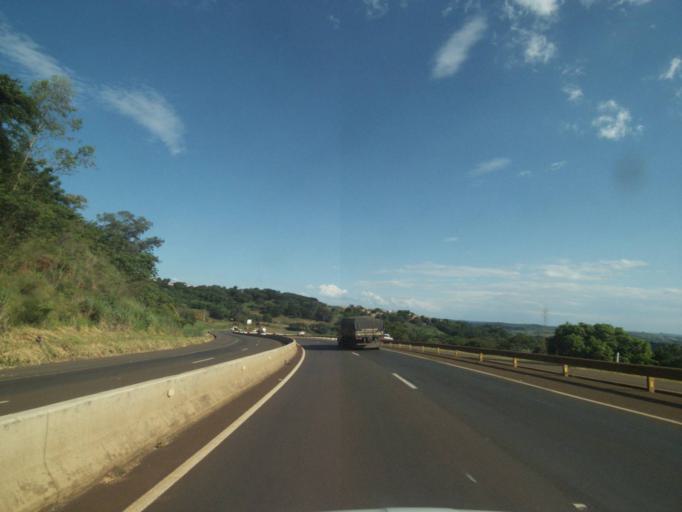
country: BR
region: Parana
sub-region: Londrina
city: Londrina
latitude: -23.3793
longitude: -51.1367
